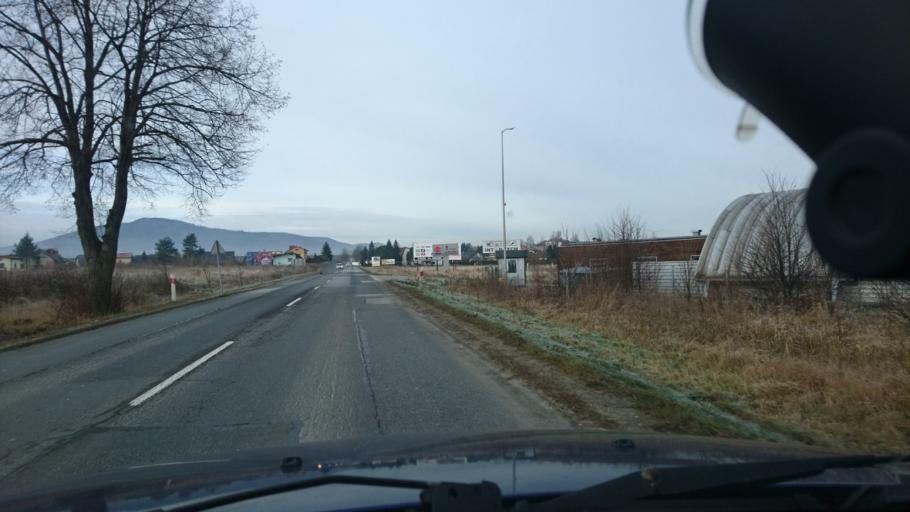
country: PL
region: Silesian Voivodeship
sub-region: Powiat zywiecki
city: Lodygowice
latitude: 49.7305
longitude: 19.1277
